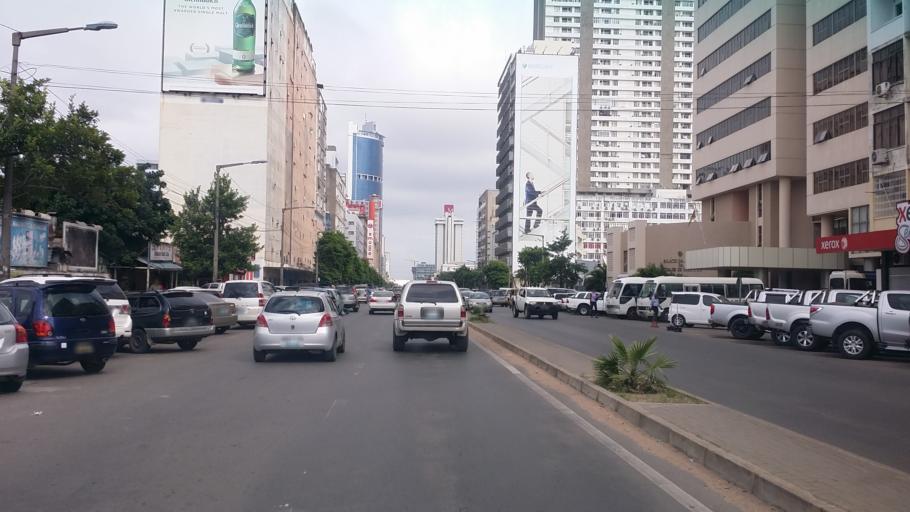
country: MZ
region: Maputo City
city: Maputo
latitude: -25.9756
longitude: 32.5758
